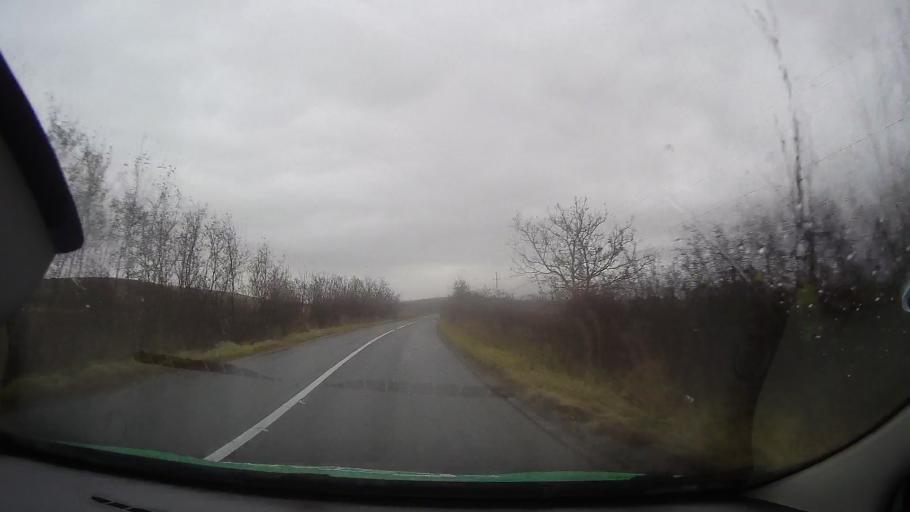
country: RO
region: Mures
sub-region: Comuna Brancovenesti
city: Valenii de Mures
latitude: 46.9043
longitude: 24.7849
